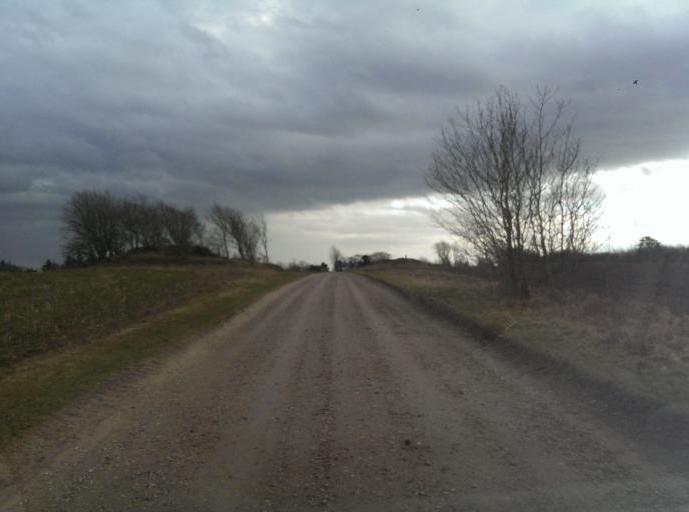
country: DK
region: South Denmark
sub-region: Esbjerg Kommune
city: Tjaereborg
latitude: 55.4792
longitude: 8.6008
